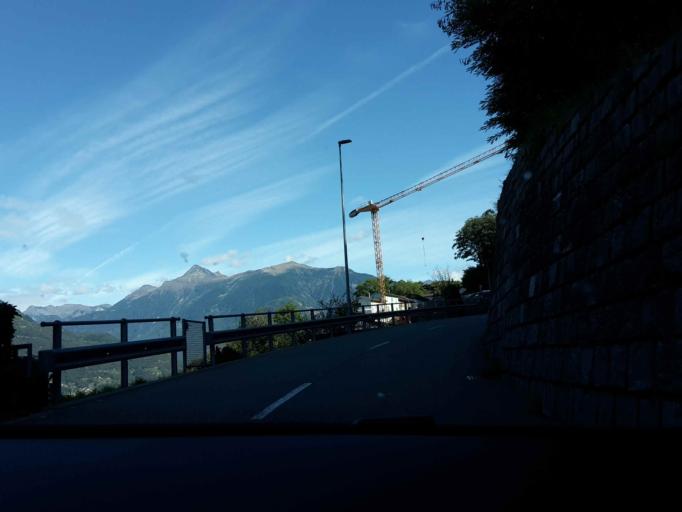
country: CH
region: Ticino
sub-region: Bellinzona District
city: Giubiasco
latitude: 46.1694
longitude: 9.0151
